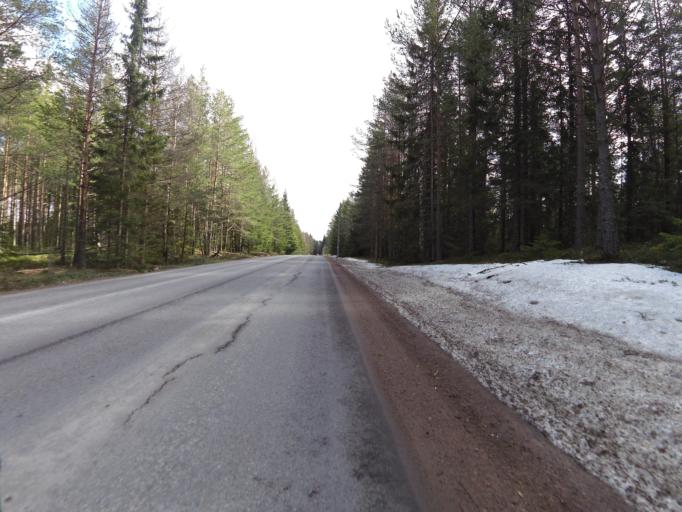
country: SE
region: Dalarna
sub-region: Hedemora Kommun
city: Brunna
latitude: 60.3155
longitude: 16.1411
